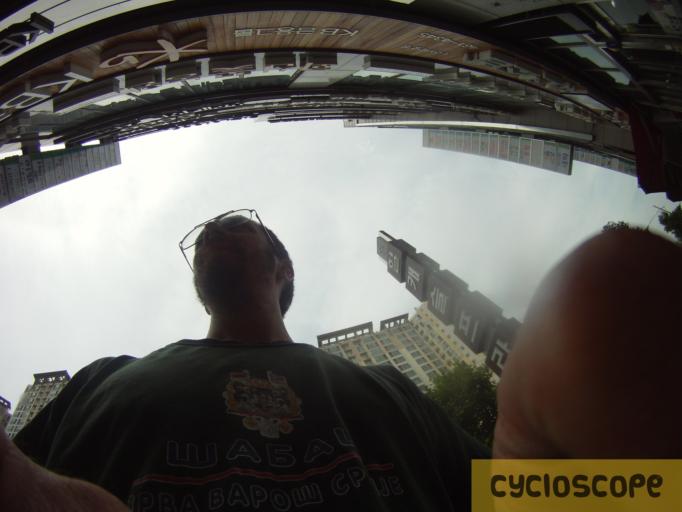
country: KR
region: Incheon
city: Incheon
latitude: 37.4561
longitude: 126.7139
